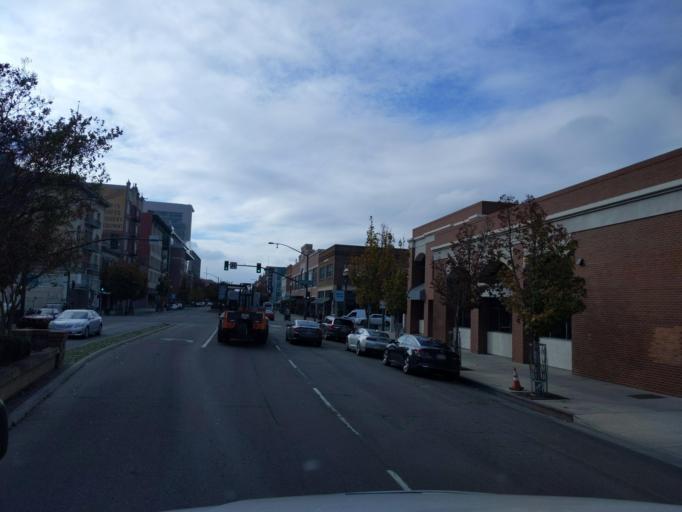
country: US
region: California
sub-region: San Joaquin County
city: Stockton
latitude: 37.9548
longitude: -121.2842
